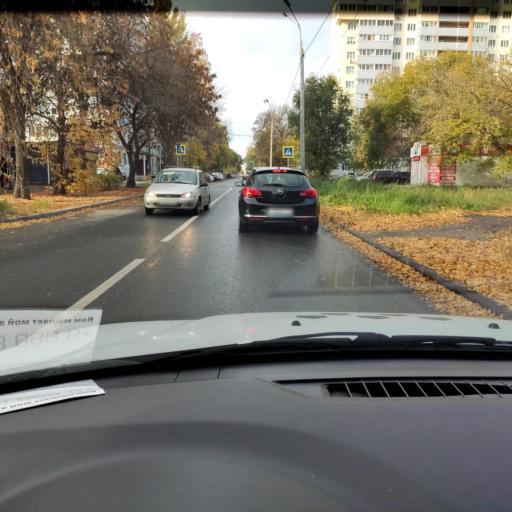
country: RU
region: Samara
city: Tol'yatti
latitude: 53.5071
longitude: 49.4272
